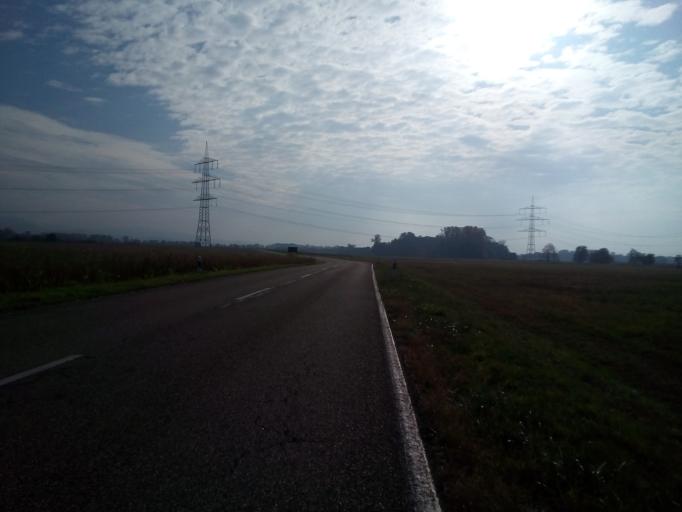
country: DE
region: Baden-Wuerttemberg
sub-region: Karlsruhe Region
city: Zell
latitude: 48.7118
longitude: 8.0686
